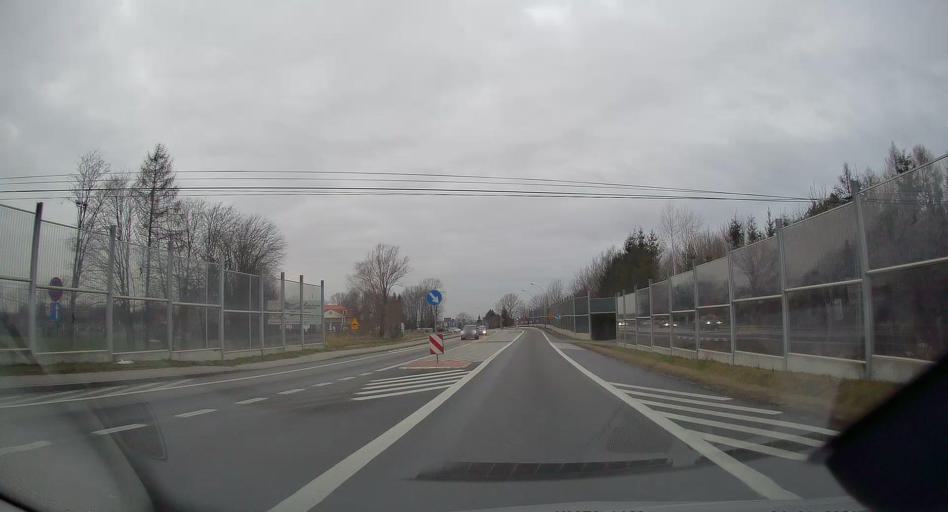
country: PL
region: Subcarpathian Voivodeship
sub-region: Powiat rzeszowski
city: Swilcza
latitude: 50.0709
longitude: 21.9064
